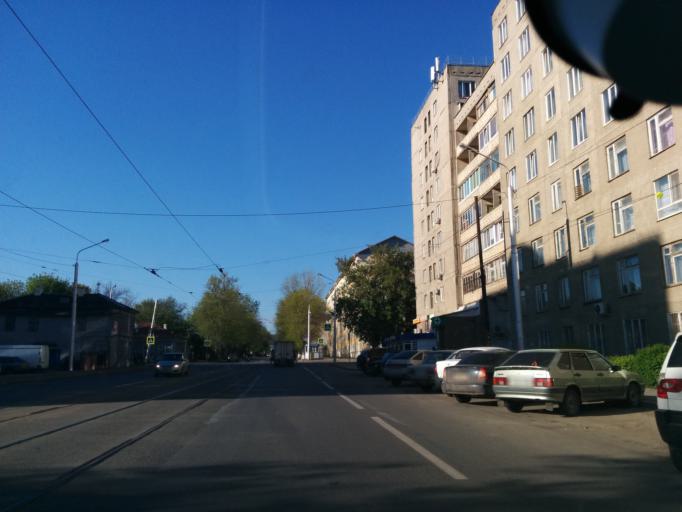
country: RU
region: Bashkortostan
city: Ufa
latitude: 54.7271
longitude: 55.9351
